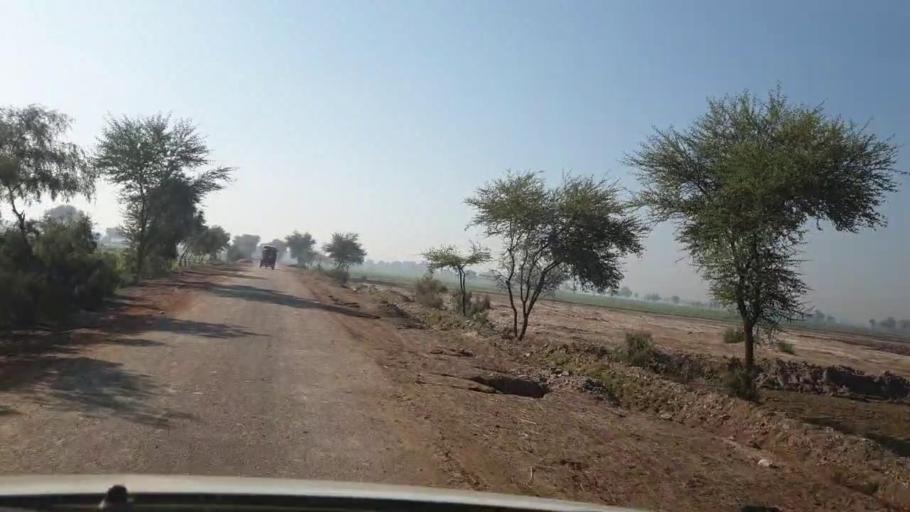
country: PK
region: Sindh
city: Dadu
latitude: 26.6465
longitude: 67.8219
